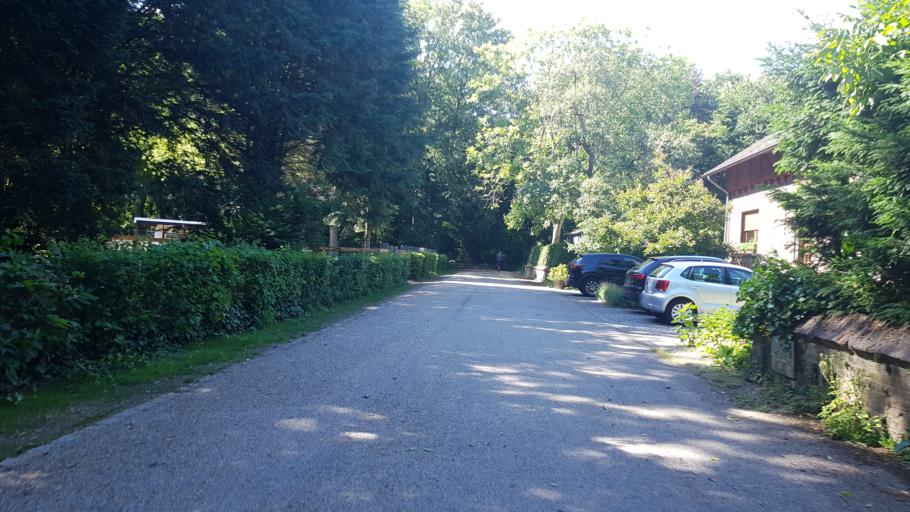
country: DE
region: North Rhine-Westphalia
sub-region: Regierungsbezirk Dusseldorf
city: Duisburg
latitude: 51.4056
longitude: 6.8088
